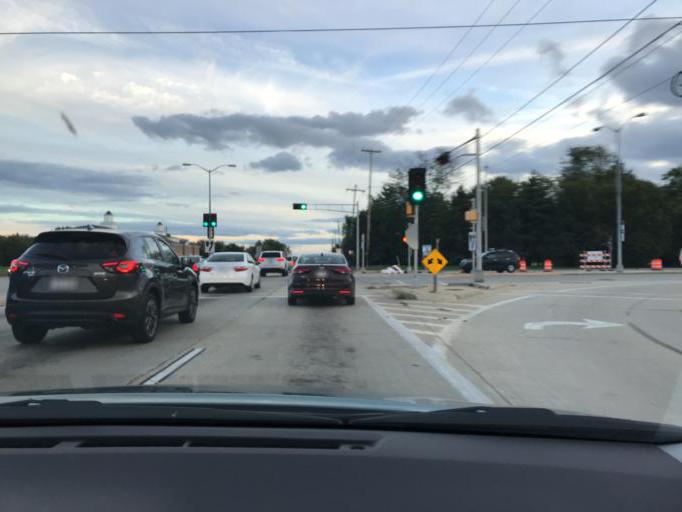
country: US
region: Wisconsin
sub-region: Kenosha County
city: Pleasant Prairie
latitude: 42.5819
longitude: -87.8842
